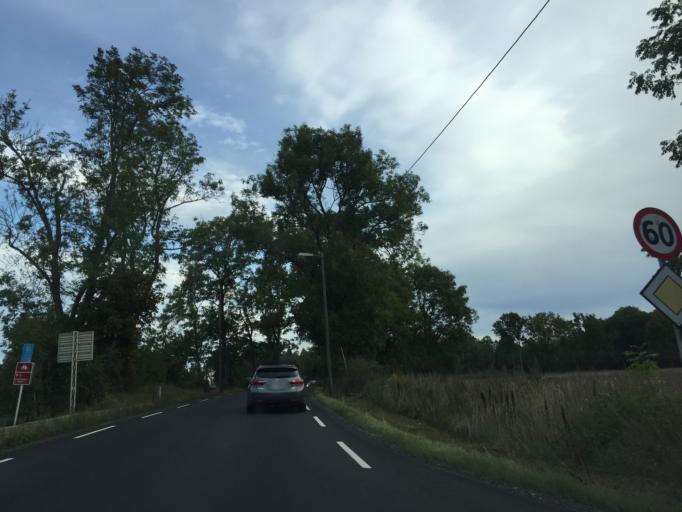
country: NO
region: Akershus
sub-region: As
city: As
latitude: 59.7070
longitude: 10.7712
